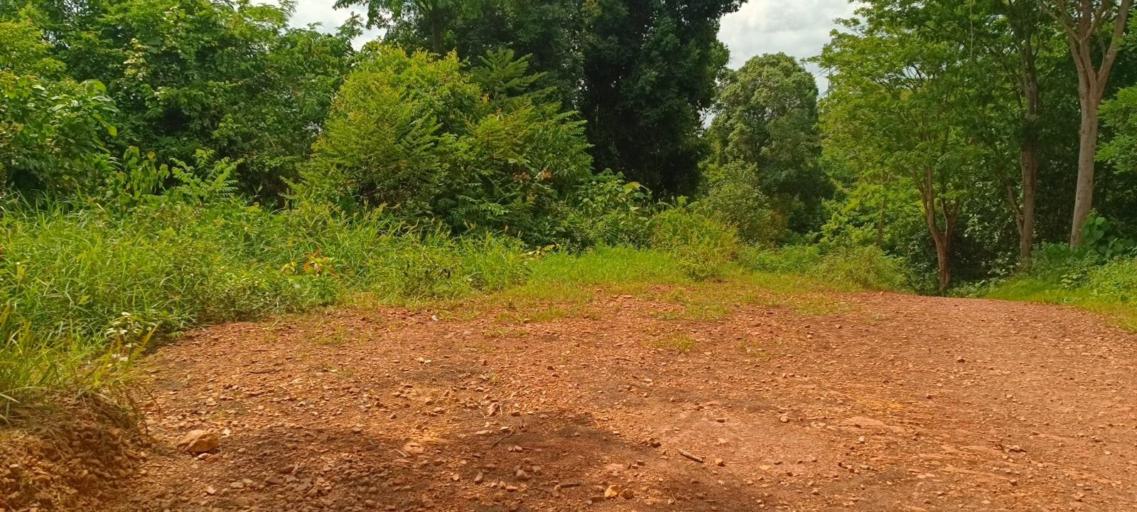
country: MY
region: Kedah
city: Sungai Petani
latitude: 5.6040
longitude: 100.4562
